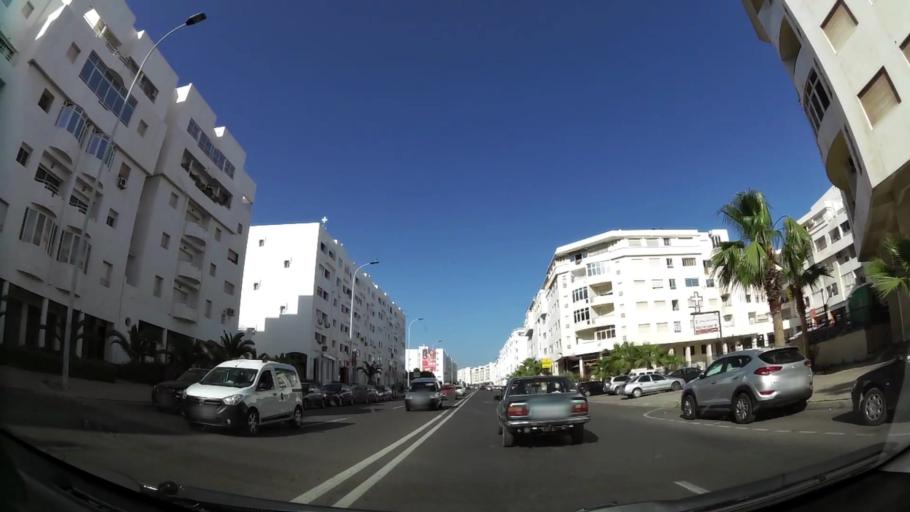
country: MA
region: Souss-Massa-Draa
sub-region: Agadir-Ida-ou-Tnan
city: Agadir
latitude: 30.4299
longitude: -9.5879
